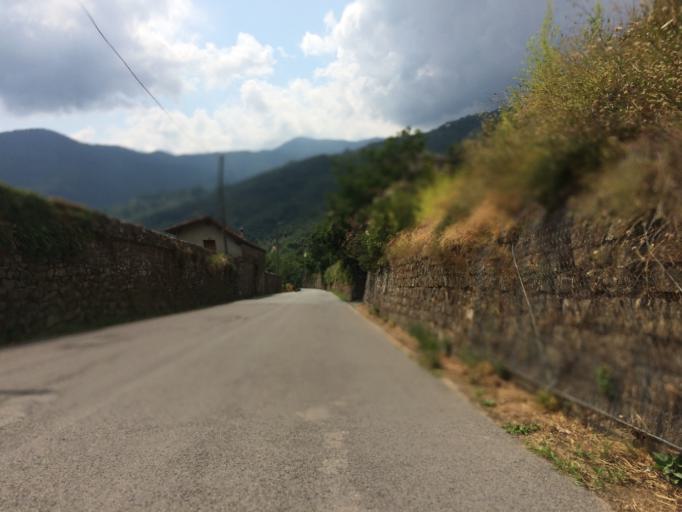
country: IT
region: Liguria
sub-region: Provincia di Imperia
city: Pigna
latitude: 43.9324
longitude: 7.6594
